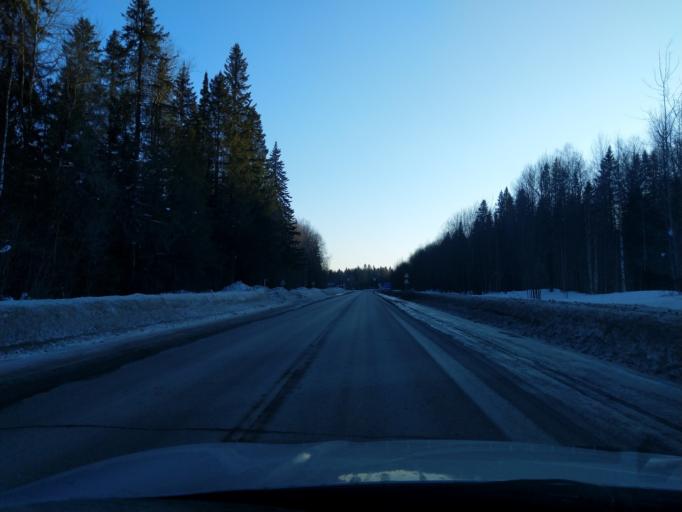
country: RU
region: Perm
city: Dobryanka
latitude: 58.4466
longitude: 56.5425
